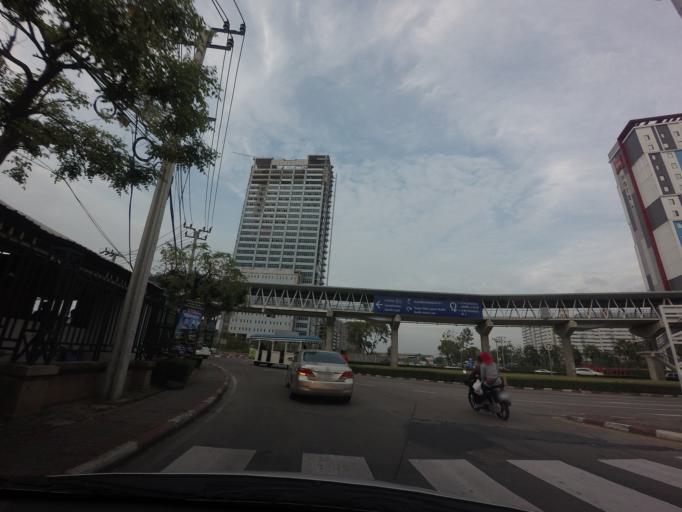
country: TH
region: Bangkok
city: Don Mueang
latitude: 13.9157
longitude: 100.5511
